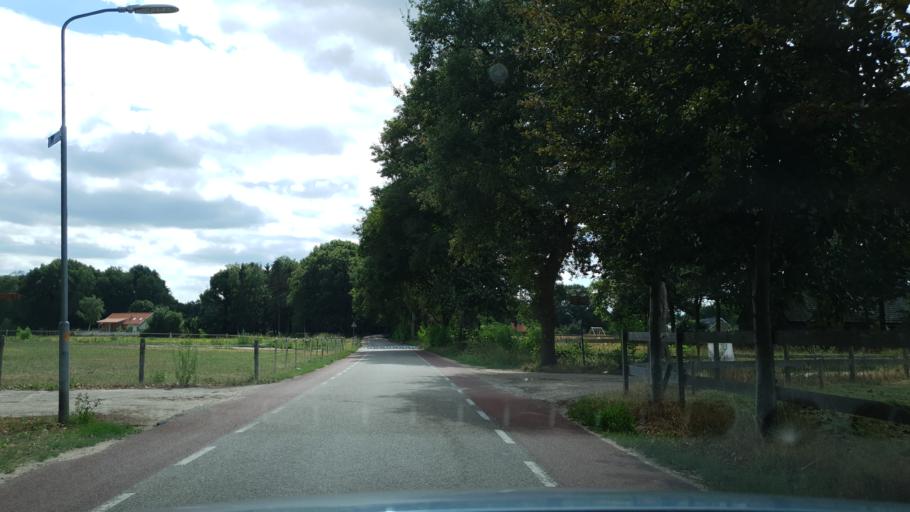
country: NL
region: Gelderland
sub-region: Gemeente Nijmegen
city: Lindenholt
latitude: 51.7796
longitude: 5.8185
